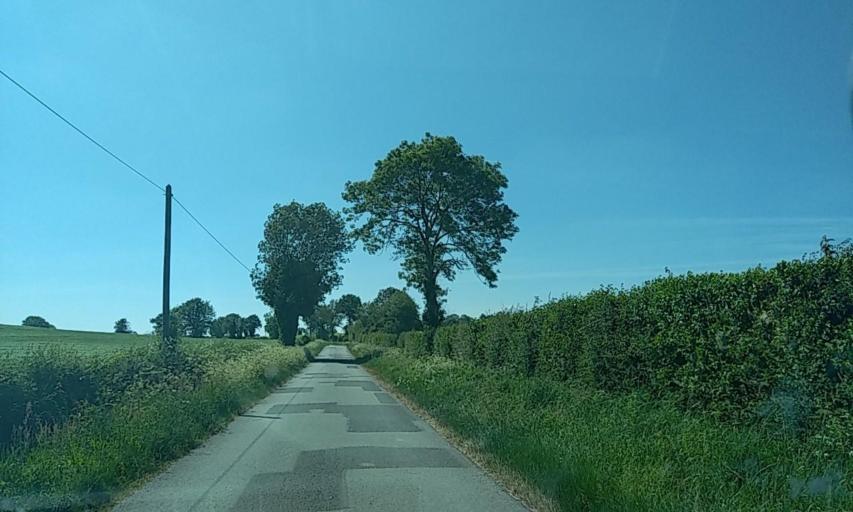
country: FR
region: Poitou-Charentes
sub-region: Departement des Deux-Sevres
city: La Chapelle-Saint-Laurent
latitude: 46.7702
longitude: -0.4756
